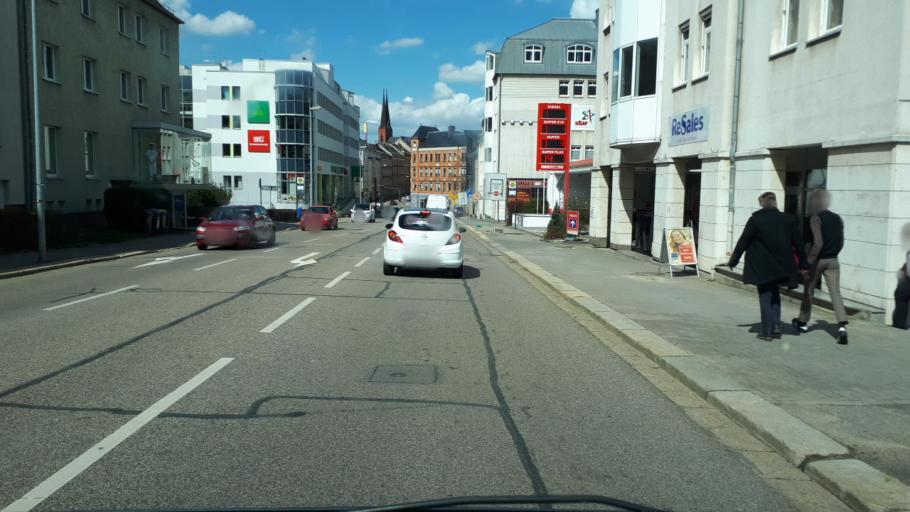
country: DE
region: Saxony
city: Chemnitz
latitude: 50.8290
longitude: 12.9402
